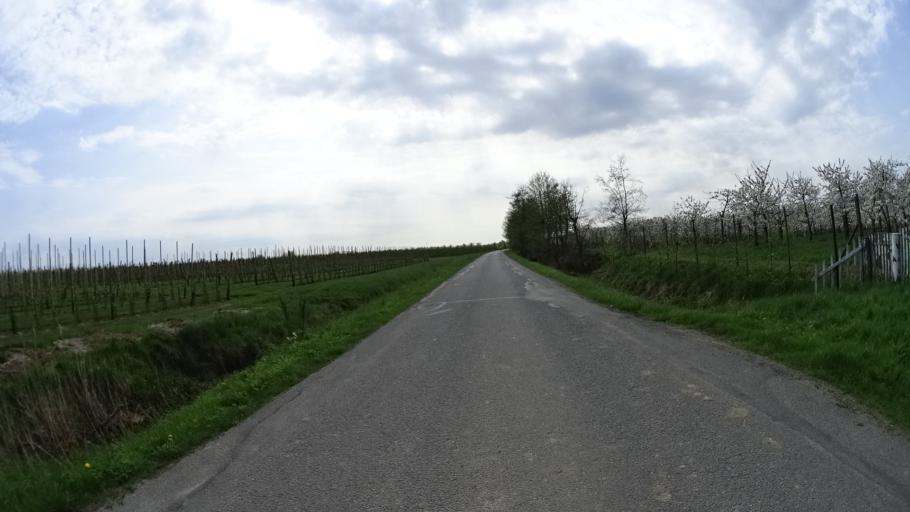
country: DE
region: Schleswig-Holstein
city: Wedel
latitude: 53.5444
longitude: 9.7422
